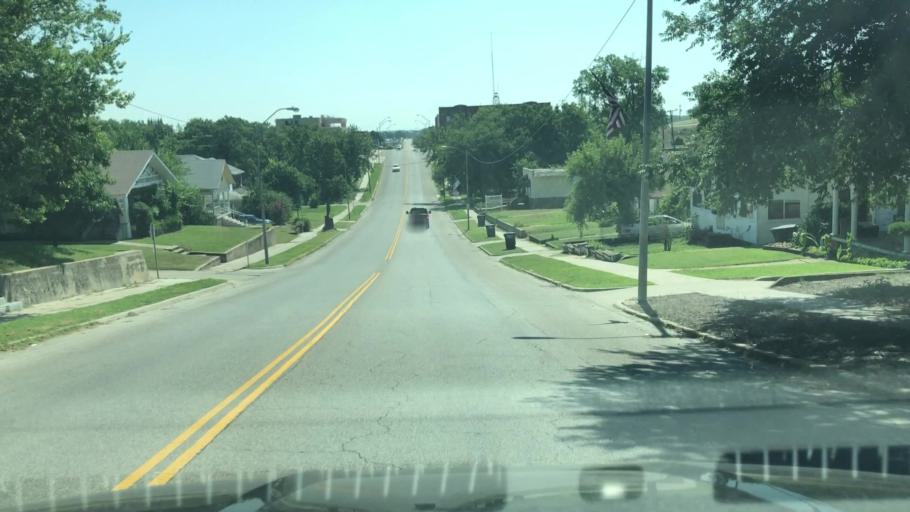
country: US
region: Oklahoma
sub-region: Creek County
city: Drumright
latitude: 35.9885
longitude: -96.6057
